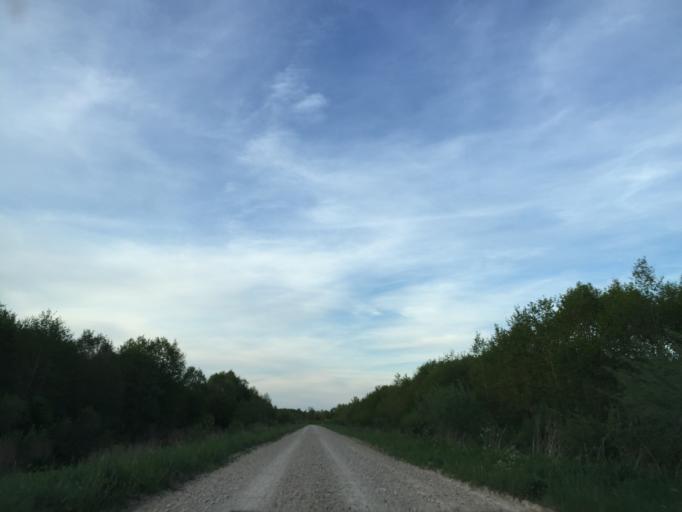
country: LV
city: Tireli
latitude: 56.7490
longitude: 23.5312
